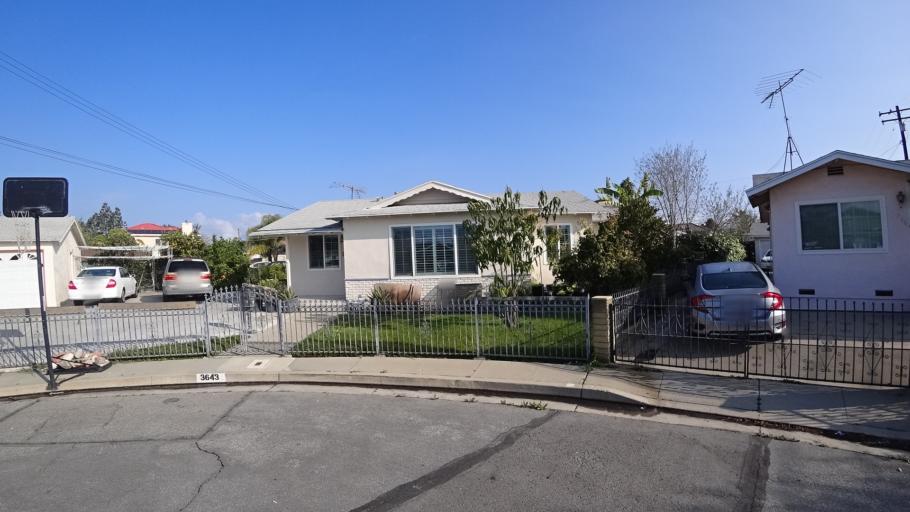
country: US
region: California
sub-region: Los Angeles County
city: Baldwin Park
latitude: 34.0779
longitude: -117.9519
